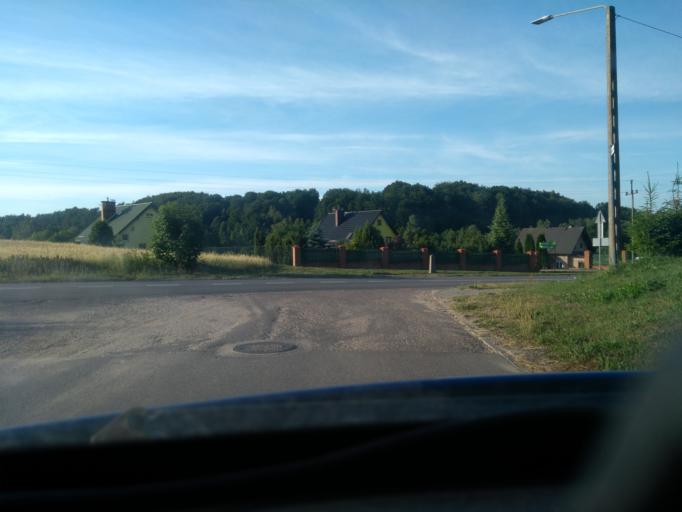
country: PL
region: Pomeranian Voivodeship
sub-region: Powiat kartuski
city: Przodkowo
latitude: 54.3811
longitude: 18.3174
